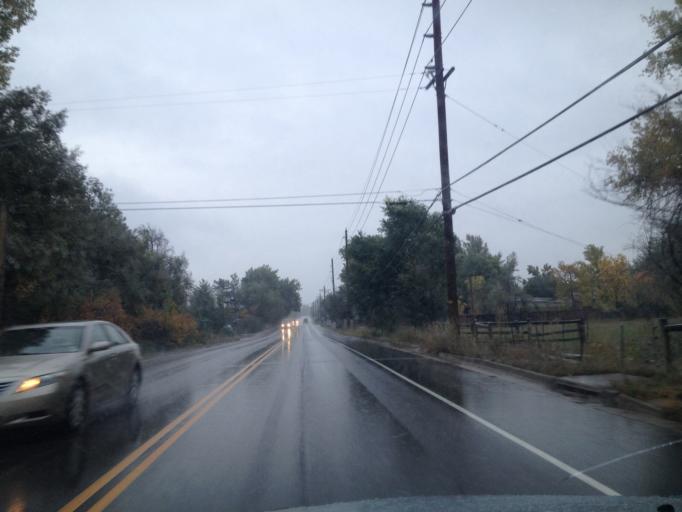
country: US
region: Colorado
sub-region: Boulder County
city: Superior
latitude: 39.9914
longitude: -105.1752
